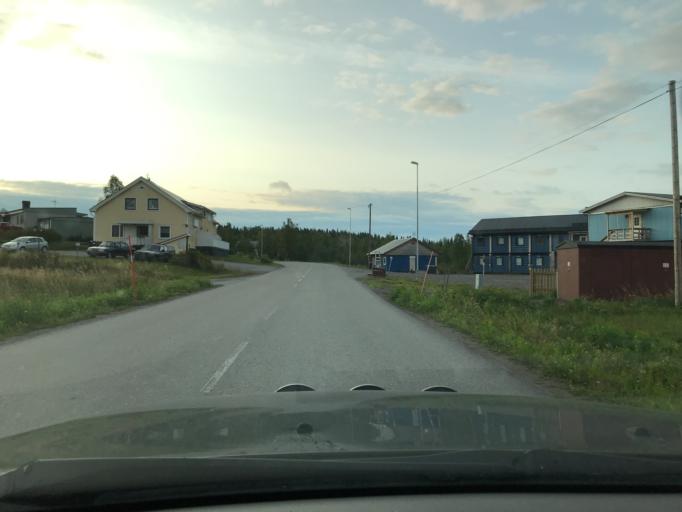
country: SE
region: Norrbotten
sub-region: Gallivare Kommun
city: Malmberget
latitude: 67.6456
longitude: 21.0525
